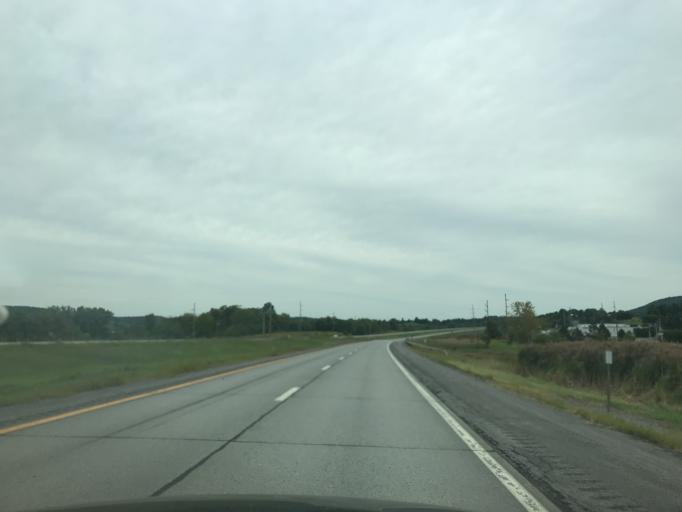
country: US
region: New York
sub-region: Schoharie County
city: Cobleskill
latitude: 42.6704
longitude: -74.4839
